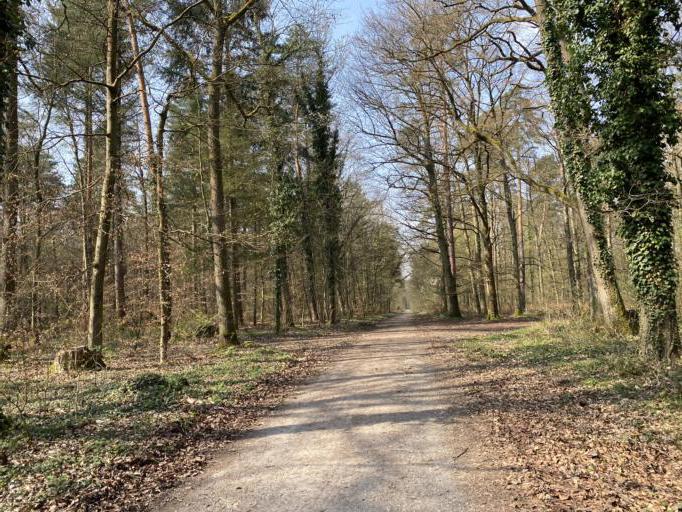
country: DE
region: Baden-Wuerttemberg
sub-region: Karlsruhe Region
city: Karlsruhe
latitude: 49.0480
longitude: 8.4128
